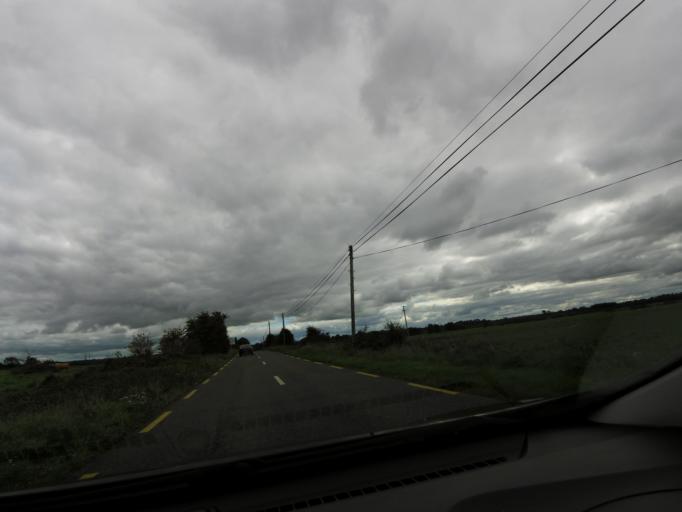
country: IE
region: Connaught
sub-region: County Galway
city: Ballinasloe
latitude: 53.2892
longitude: -8.0869
